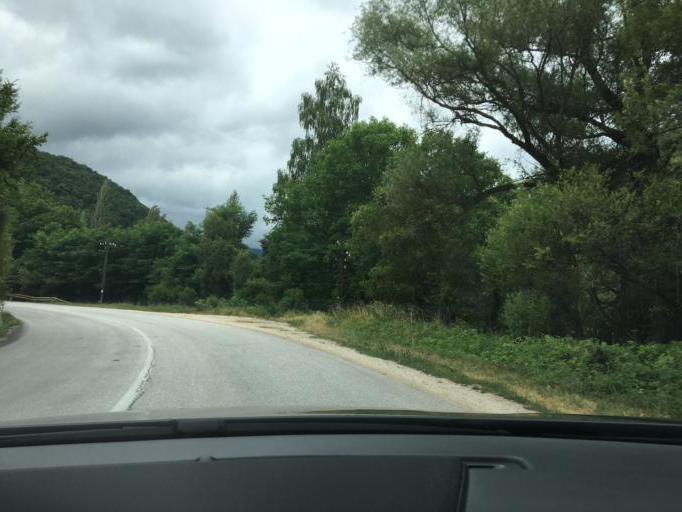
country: MK
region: Kriva Palanka
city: Kriva Palanka
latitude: 42.2264
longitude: 22.3587
